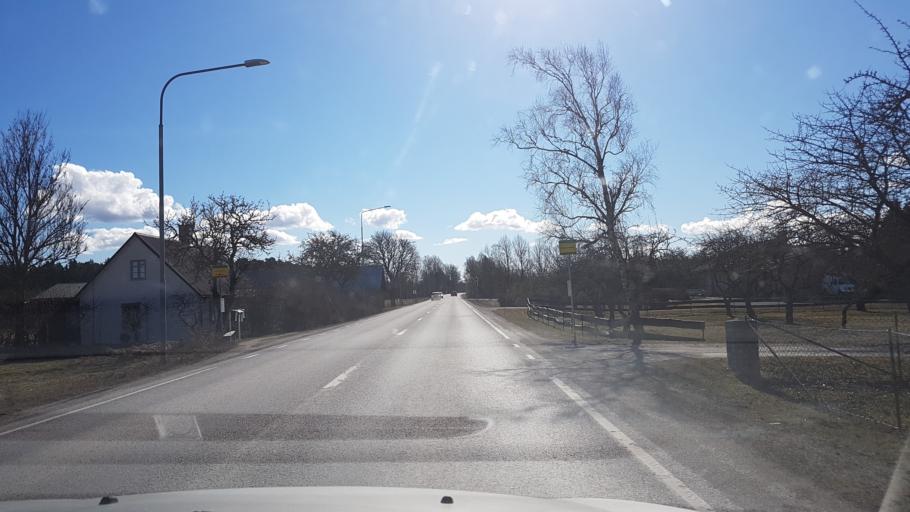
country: SE
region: Gotland
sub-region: Gotland
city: Visby
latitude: 57.5225
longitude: 18.4419
